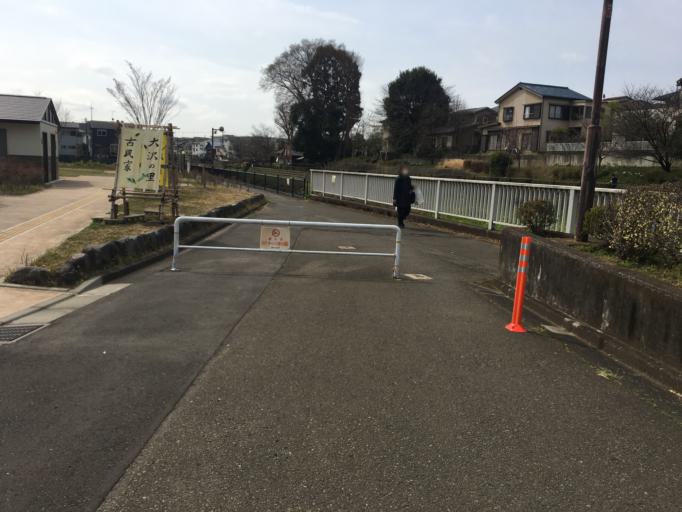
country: JP
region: Tokyo
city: Chofugaoka
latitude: 35.6788
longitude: 139.5307
